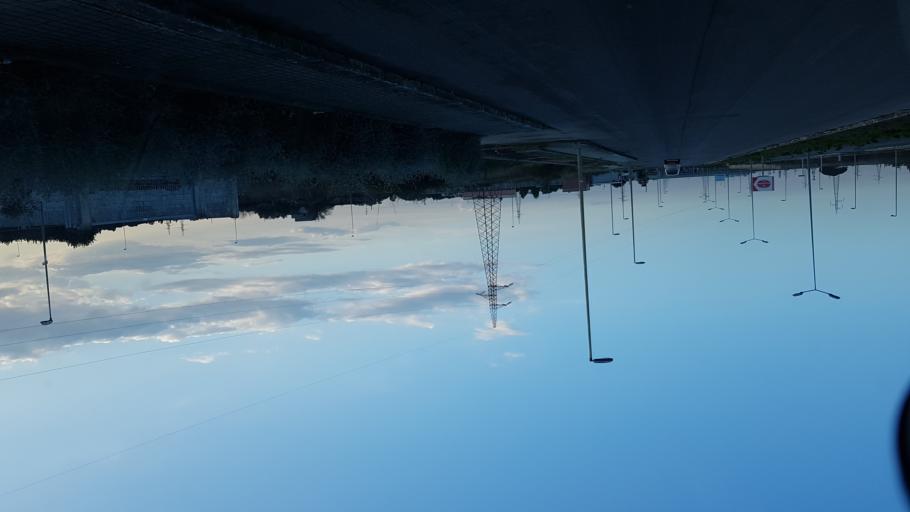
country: IT
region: Apulia
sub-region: Provincia di Lecce
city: Giorgilorio
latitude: 40.3726
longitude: 18.1376
